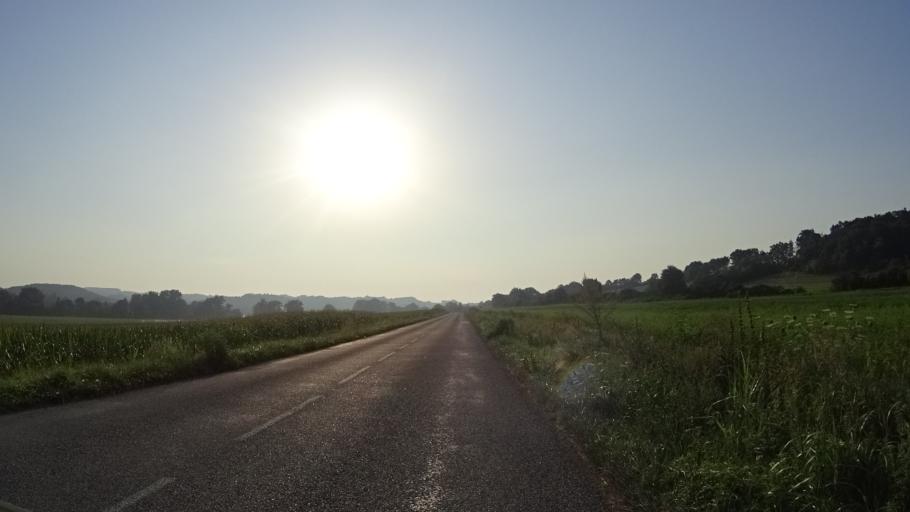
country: FR
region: Midi-Pyrenees
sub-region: Departement de l'Ariege
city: Mirepoix
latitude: 43.0858
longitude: 1.9173
